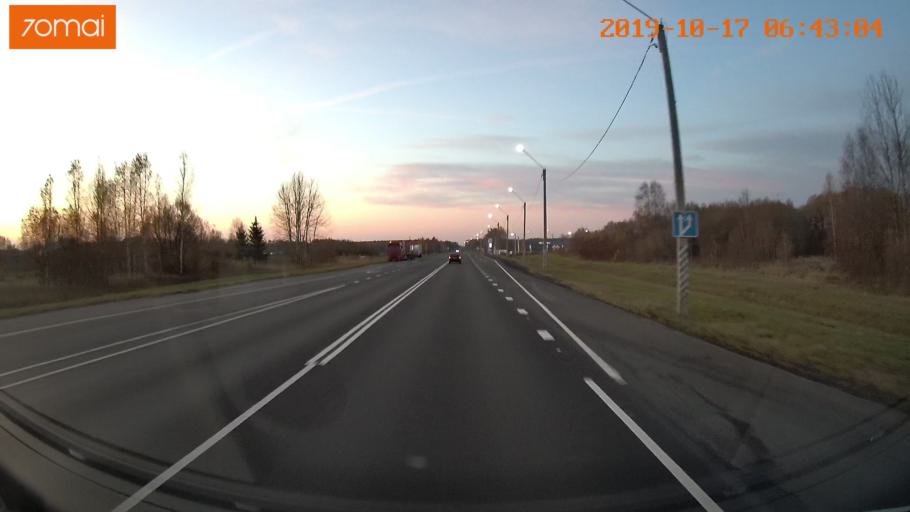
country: RU
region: Vladimir
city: Kideksha
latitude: 56.5925
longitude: 40.5554
